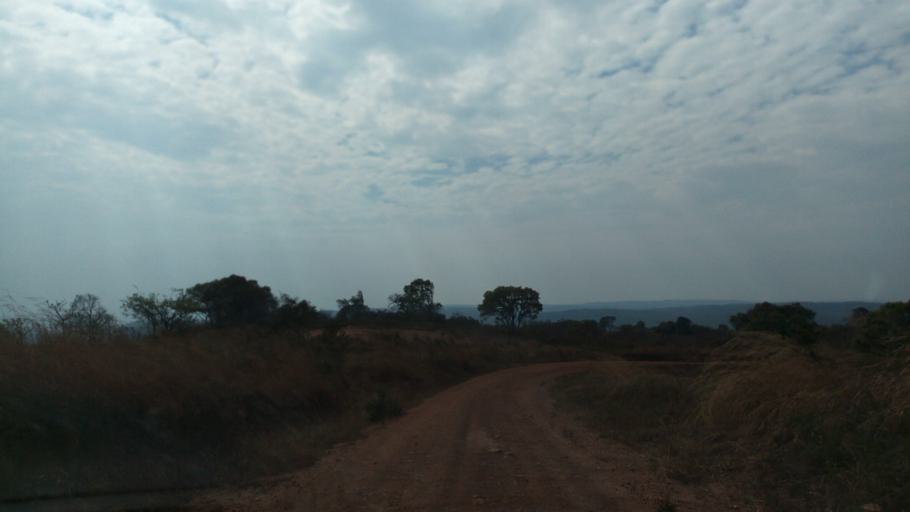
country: CD
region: Katanga
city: Kalemie
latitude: -6.2047
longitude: 28.9087
